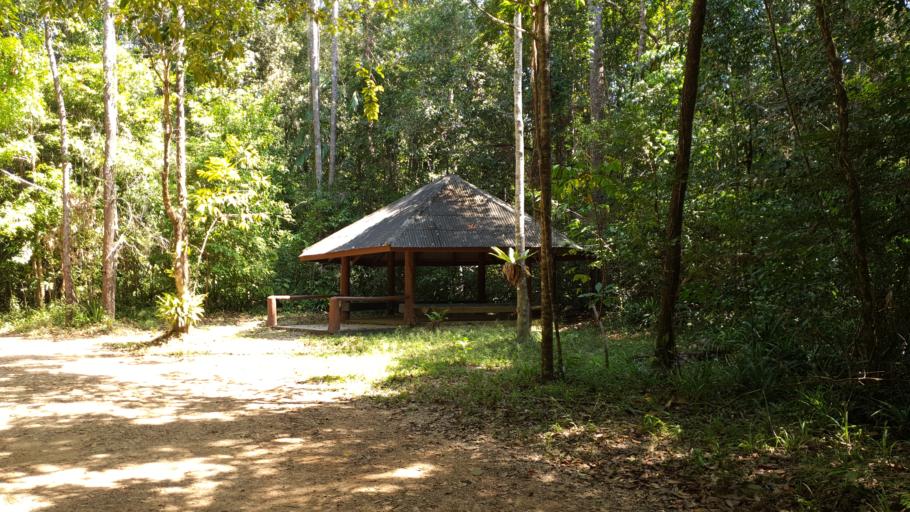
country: TH
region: Krabi
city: Khlong Thom
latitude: 7.9253
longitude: 99.2629
